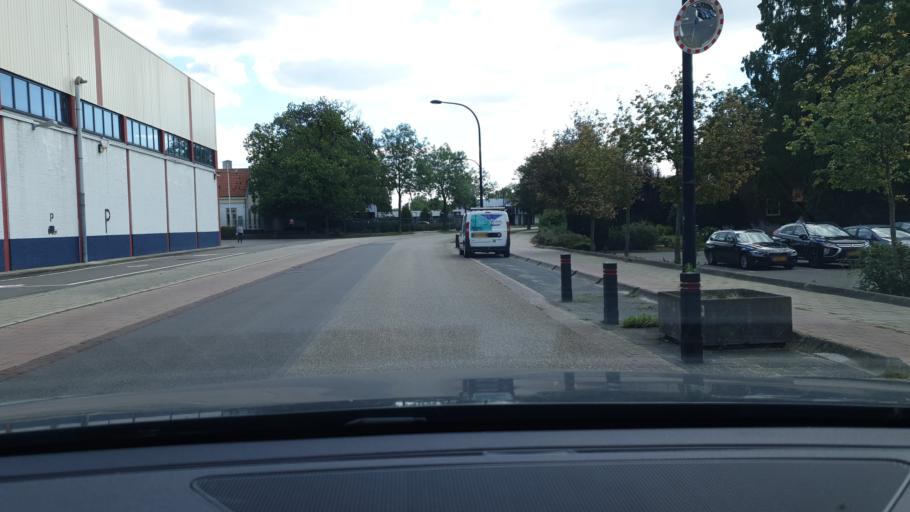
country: NL
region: North Brabant
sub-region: Gemeente Cuijk
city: Cuijk
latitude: 51.7242
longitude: 5.8859
